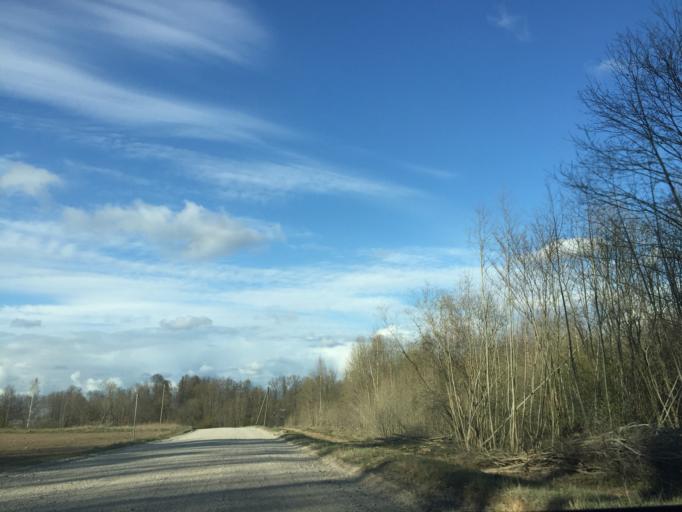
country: LV
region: Burtnieki
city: Matisi
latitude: 57.6104
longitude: 25.0749
